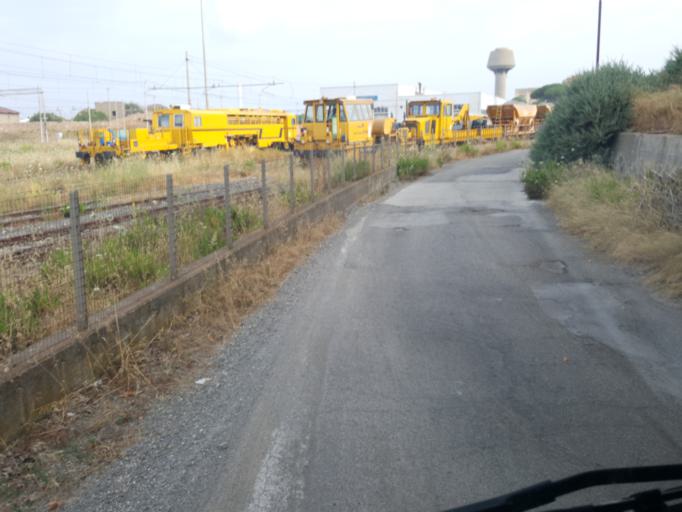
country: IT
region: Latium
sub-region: Citta metropolitana di Roma Capitale
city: Civitavecchia
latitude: 42.0993
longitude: 11.7899
